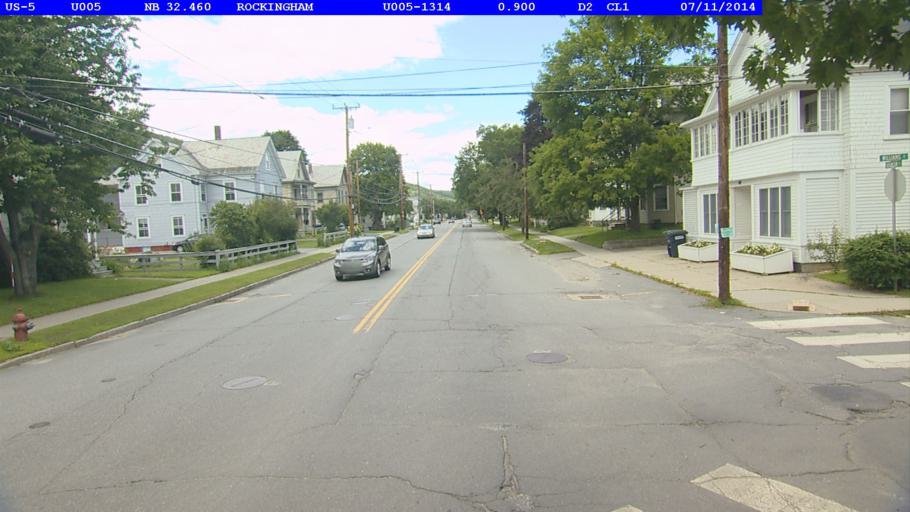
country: US
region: Vermont
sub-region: Windham County
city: Bellows Falls
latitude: 43.1356
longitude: -72.4511
